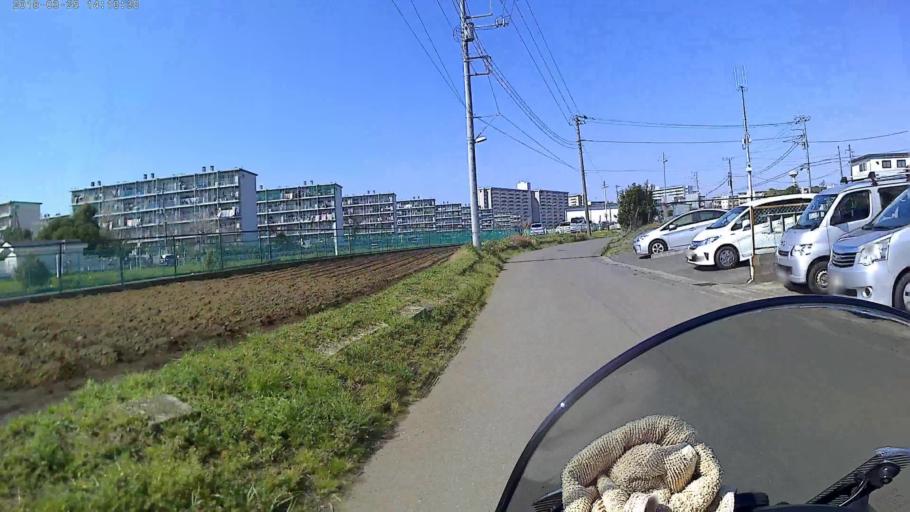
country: JP
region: Kanagawa
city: Minami-rinkan
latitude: 35.4247
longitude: 139.4733
